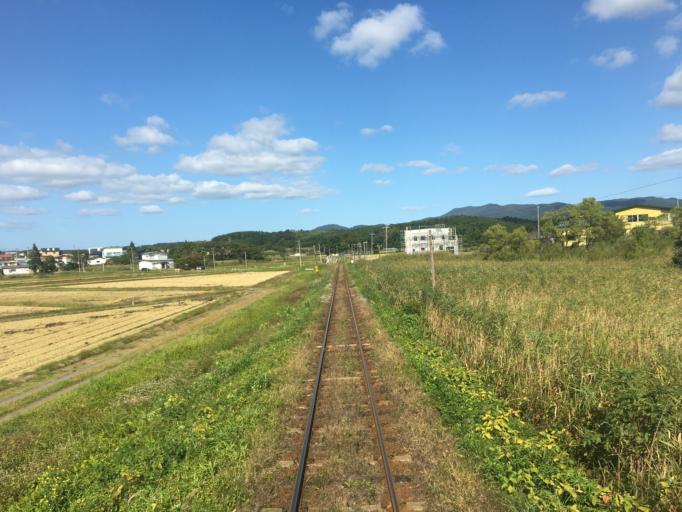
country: JP
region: Aomori
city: Goshogawara
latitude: 40.9495
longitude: 140.4392
